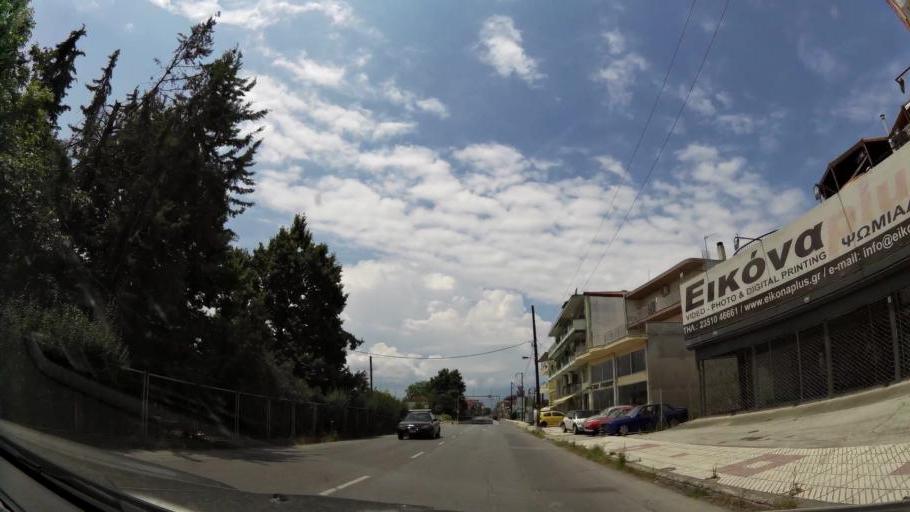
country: GR
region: Central Macedonia
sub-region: Nomos Pierias
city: Peristasi
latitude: 40.2712
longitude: 22.5342
